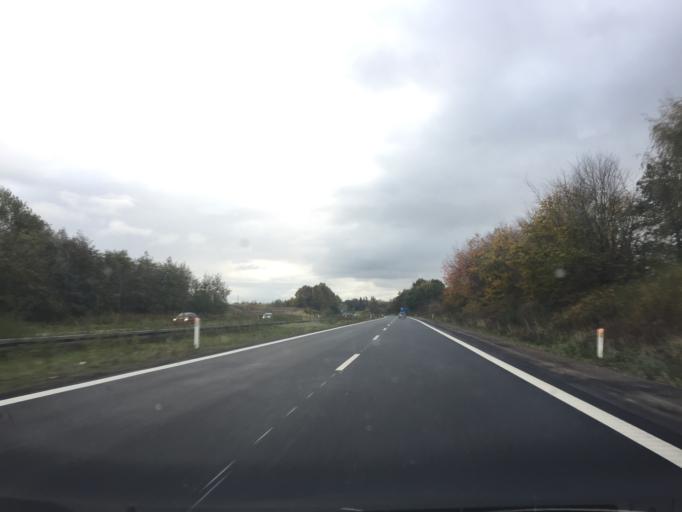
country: DK
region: Capital Region
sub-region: Fredensborg Kommune
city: Kokkedal
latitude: 55.9204
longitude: 12.4737
